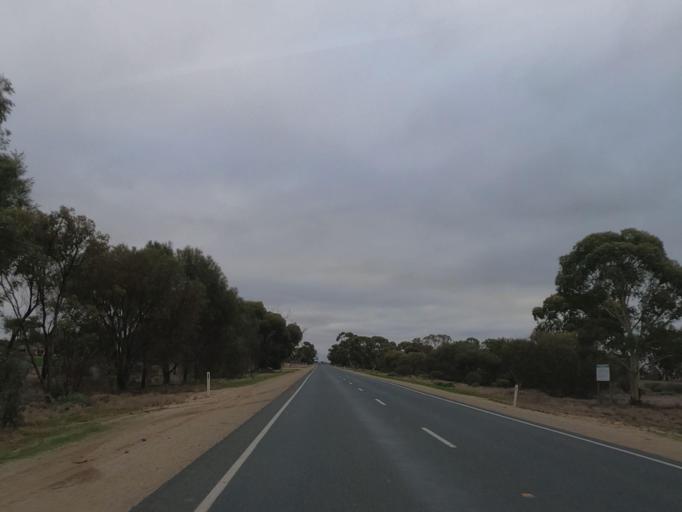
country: AU
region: Victoria
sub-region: Swan Hill
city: Swan Hill
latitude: -35.4005
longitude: 143.5769
